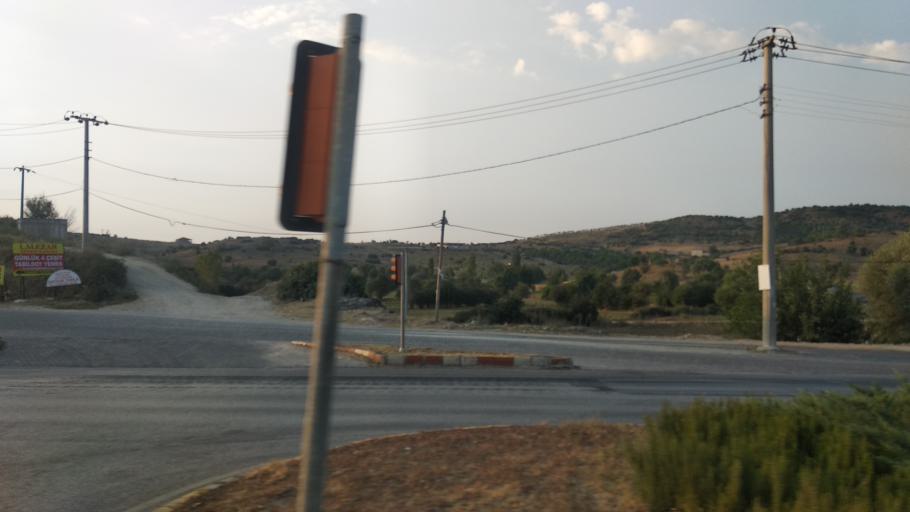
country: TR
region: Manisa
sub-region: Kula
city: Kula
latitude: 38.5461
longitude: 28.6667
